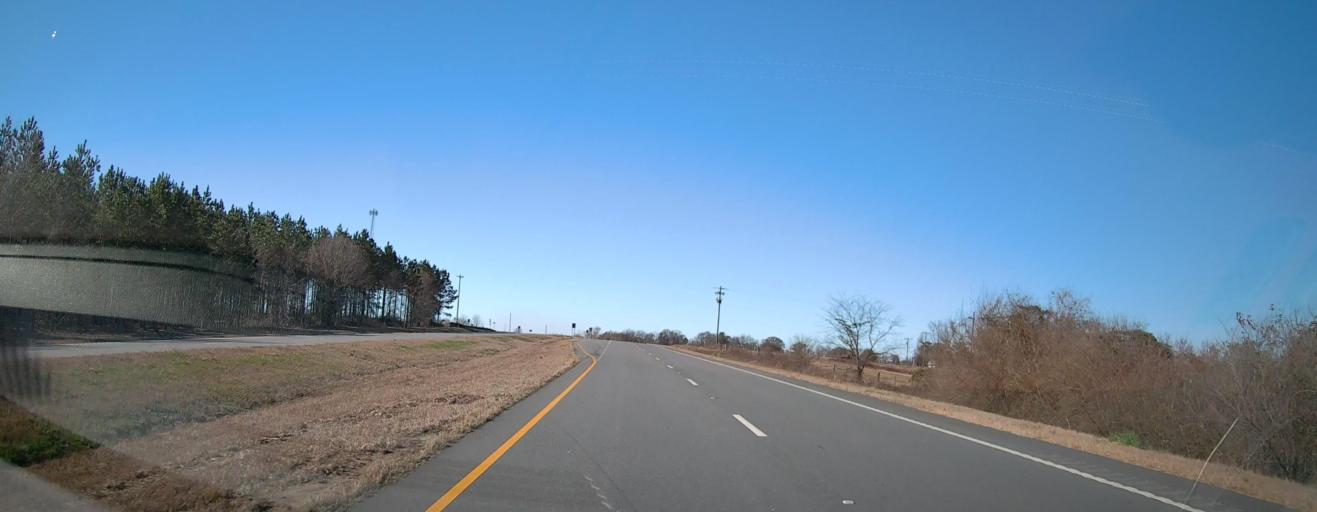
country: US
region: Georgia
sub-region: Taylor County
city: Butler
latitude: 32.6238
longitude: -84.2490
